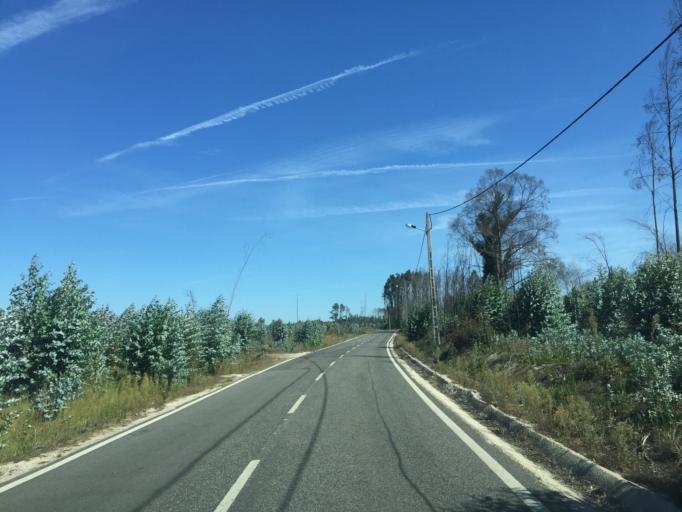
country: PT
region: Coimbra
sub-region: Figueira da Foz
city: Tavarede
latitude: 40.2199
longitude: -8.8317
